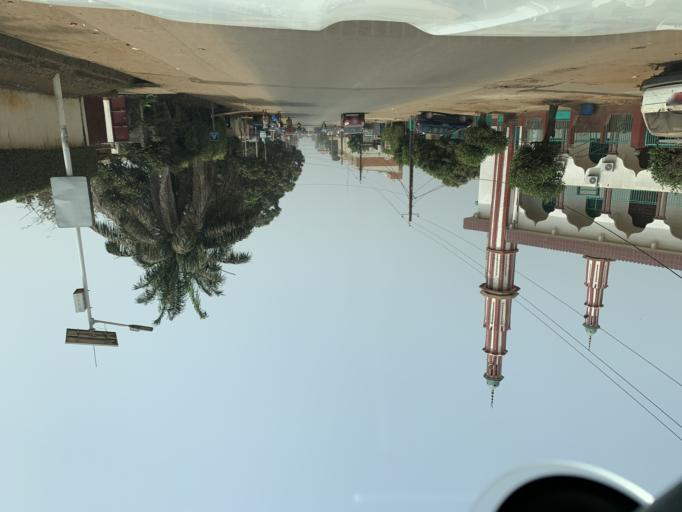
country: GN
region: Conakry
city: Camayenne
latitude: 9.5310
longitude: -13.6813
